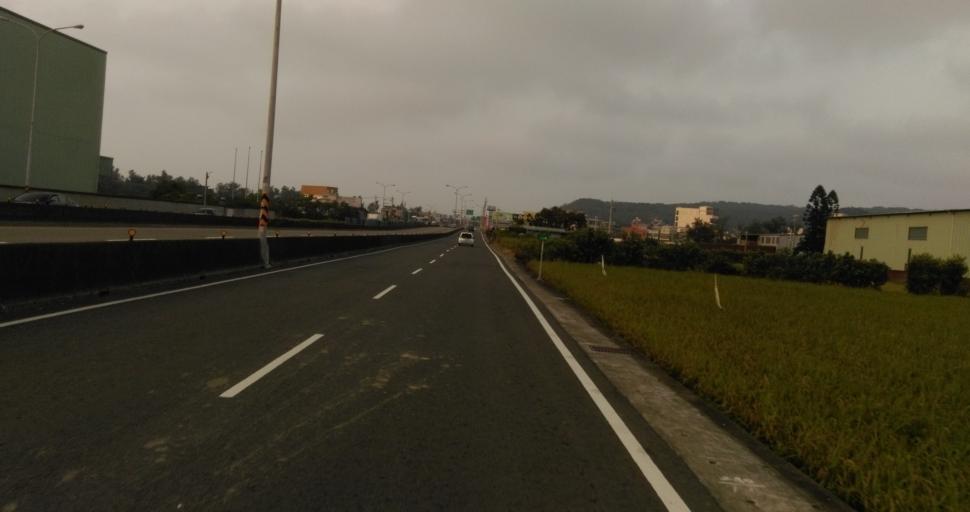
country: TW
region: Taiwan
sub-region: Hsinchu
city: Zhubei
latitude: 24.8687
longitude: 120.9536
